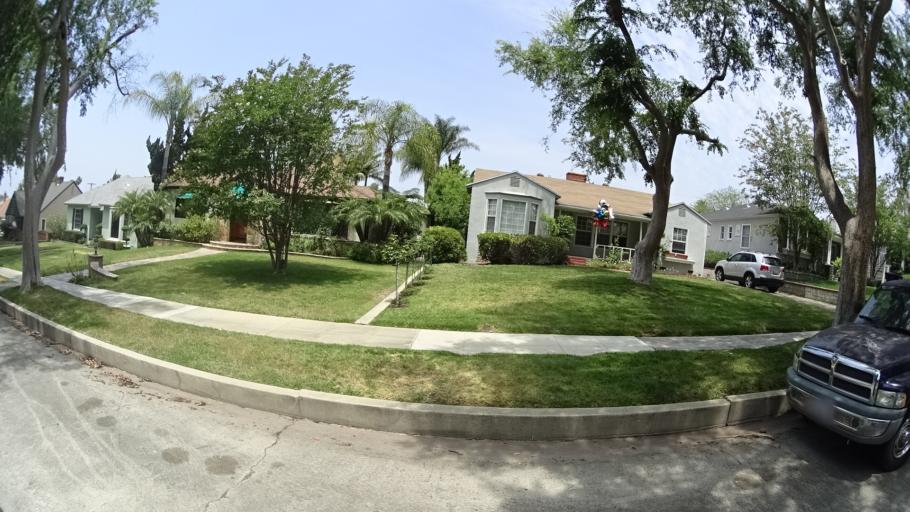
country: US
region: California
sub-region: Los Angeles County
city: Burbank
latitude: 34.1915
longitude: -118.3099
